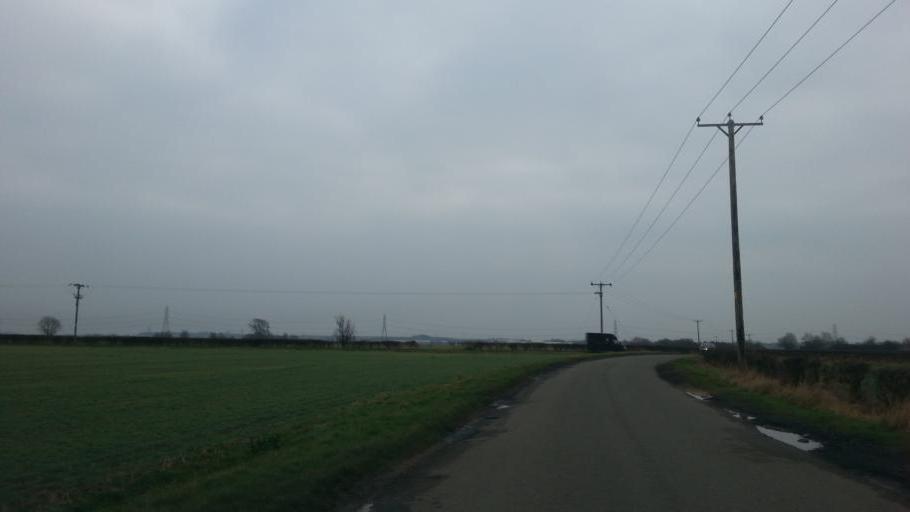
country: GB
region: England
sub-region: Lincolnshire
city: Long Bennington
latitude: 53.0043
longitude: -0.7877
